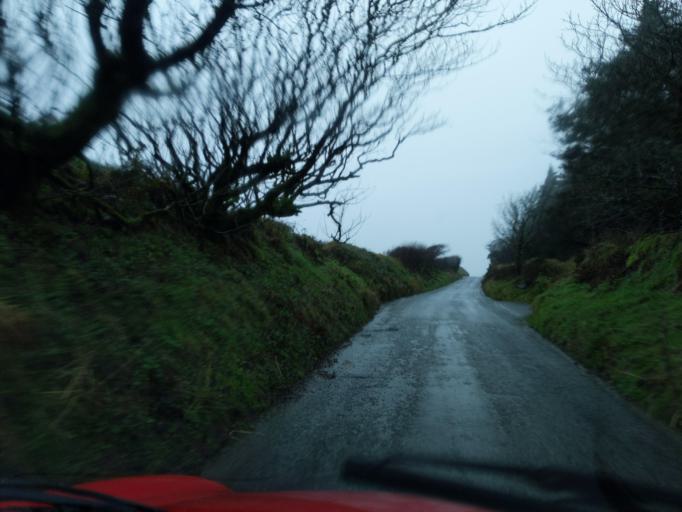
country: GB
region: England
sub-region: Cornwall
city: Camelford
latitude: 50.6494
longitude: -4.7003
